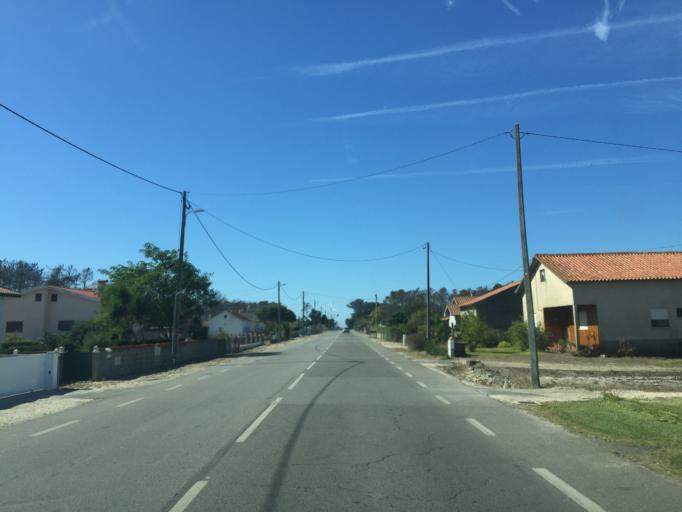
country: PT
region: Coimbra
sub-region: Mira
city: Mira
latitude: 40.3214
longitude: -8.7790
